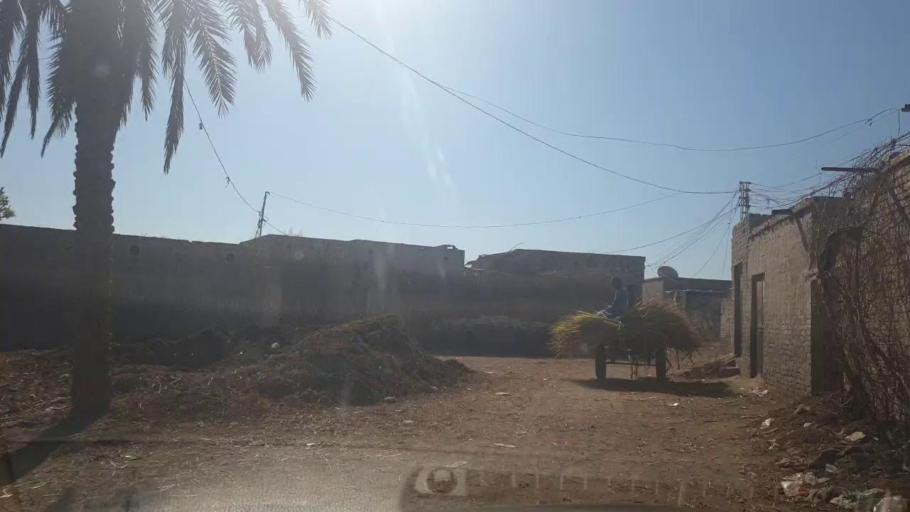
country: PK
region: Sindh
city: Adilpur
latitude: 27.9407
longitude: 69.3371
